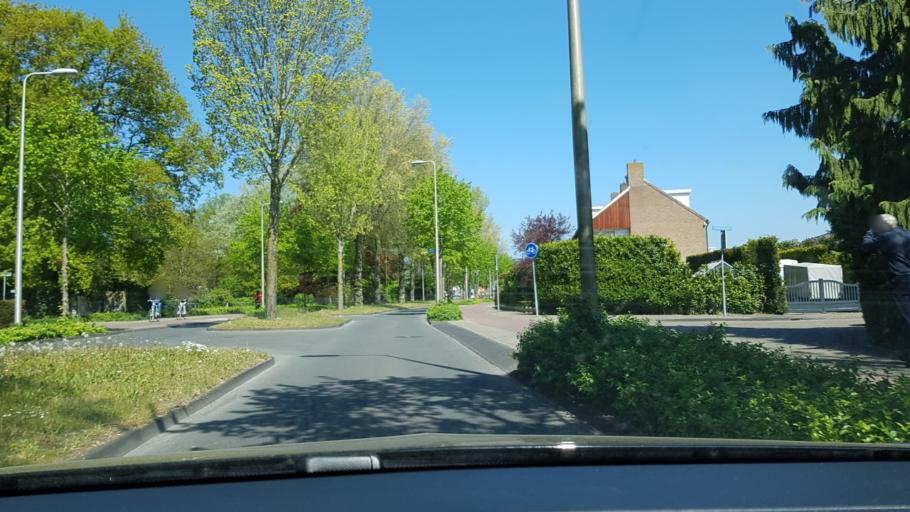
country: NL
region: North Holland
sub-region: Gemeente Bloemendaal
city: Bennebroek
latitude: 52.3268
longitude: 4.6052
